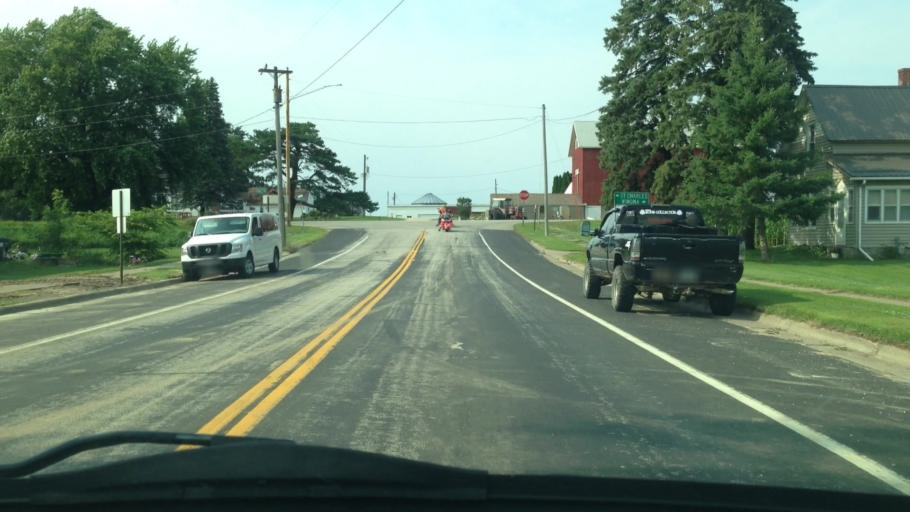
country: US
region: Minnesota
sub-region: Winona County
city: Lewiston
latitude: 43.9773
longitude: -91.9555
